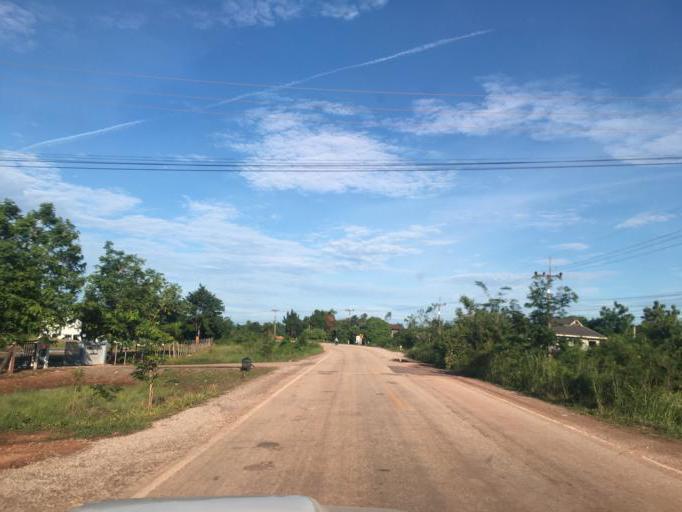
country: TH
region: Changwat Udon Thani
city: Kut Chap
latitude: 17.3831
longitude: 102.6107
